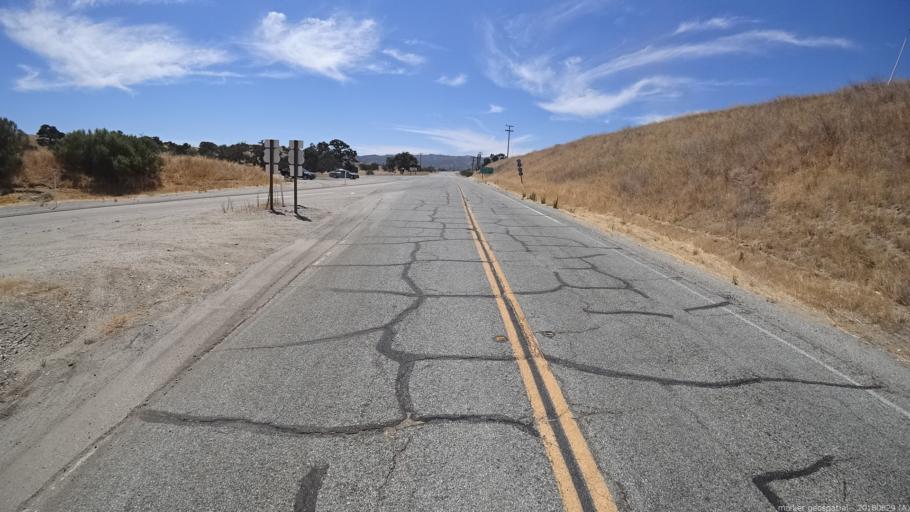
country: US
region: California
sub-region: San Luis Obispo County
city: Lake Nacimiento
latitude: 35.8733
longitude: -120.8377
